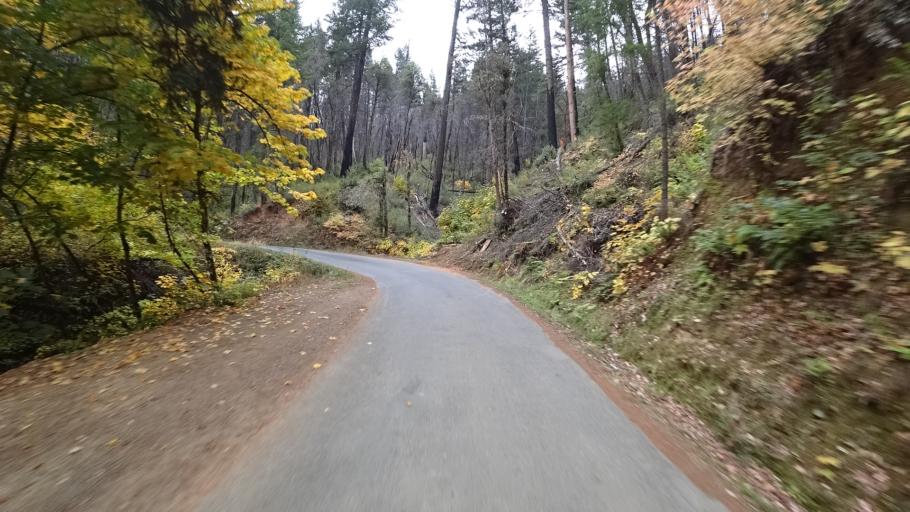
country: US
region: California
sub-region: Siskiyou County
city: Happy Camp
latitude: 41.7939
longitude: -123.3640
